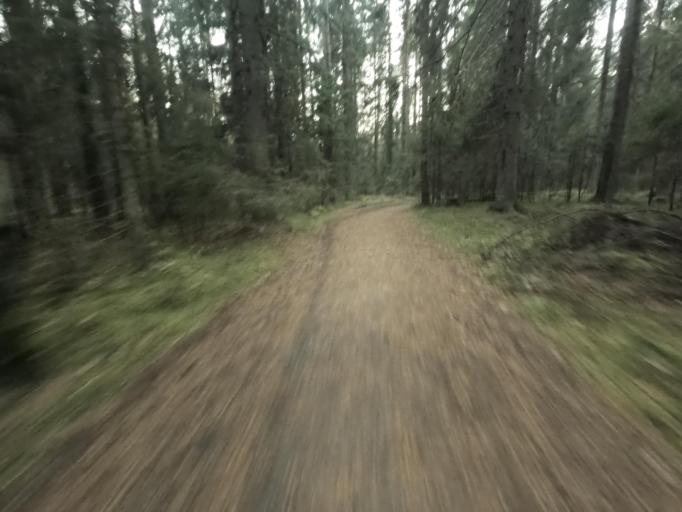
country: RU
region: Leningrad
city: Leninskoye
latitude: 60.1990
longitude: 29.8424
